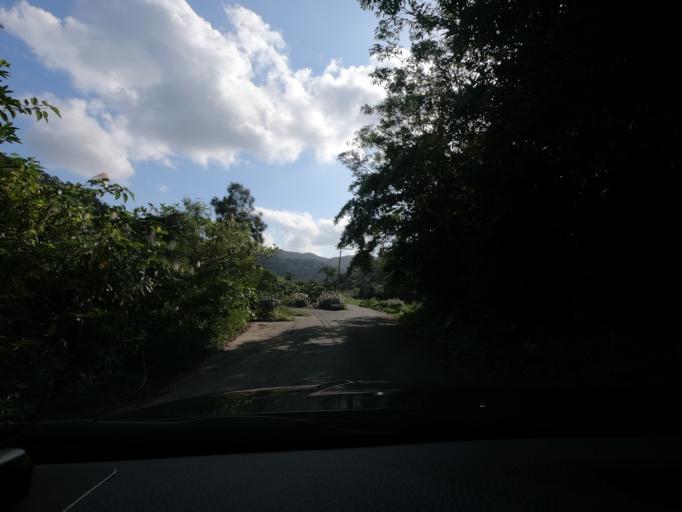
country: JP
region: Okinawa
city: Nago
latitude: 26.7656
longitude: 128.2104
